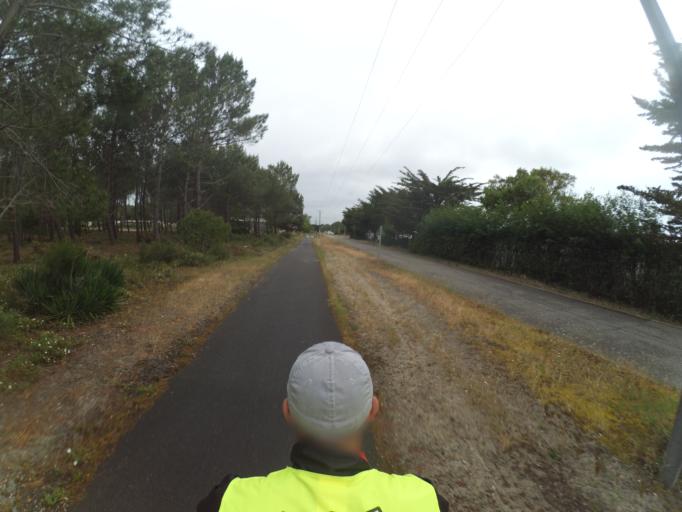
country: FR
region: Aquitaine
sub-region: Departement des Landes
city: Mimizan
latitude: 44.2180
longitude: -1.2816
